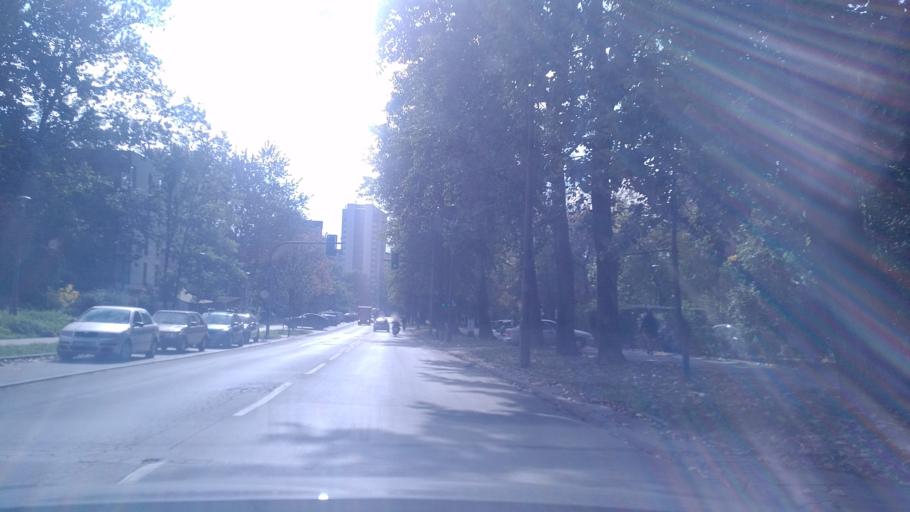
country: PL
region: Lesser Poland Voivodeship
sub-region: Krakow
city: Krakow
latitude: 50.0776
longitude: 19.9176
